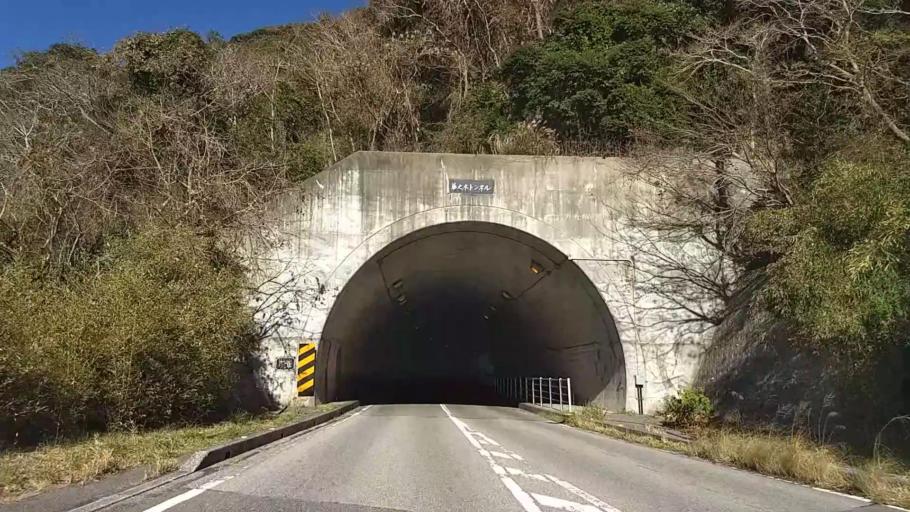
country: JP
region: Chiba
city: Katsuura
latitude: 35.1329
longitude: 140.2409
